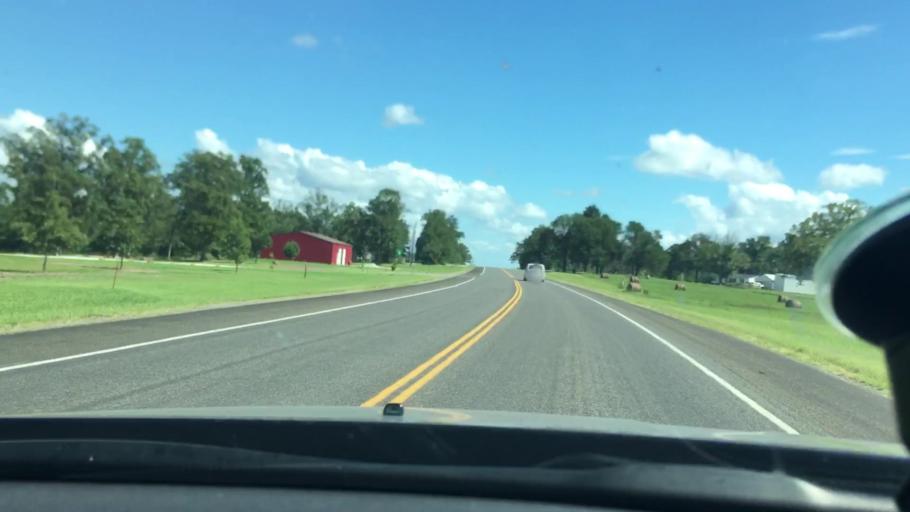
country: US
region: Oklahoma
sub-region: Sequoyah County
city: Vian
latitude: 35.5556
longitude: -94.9776
